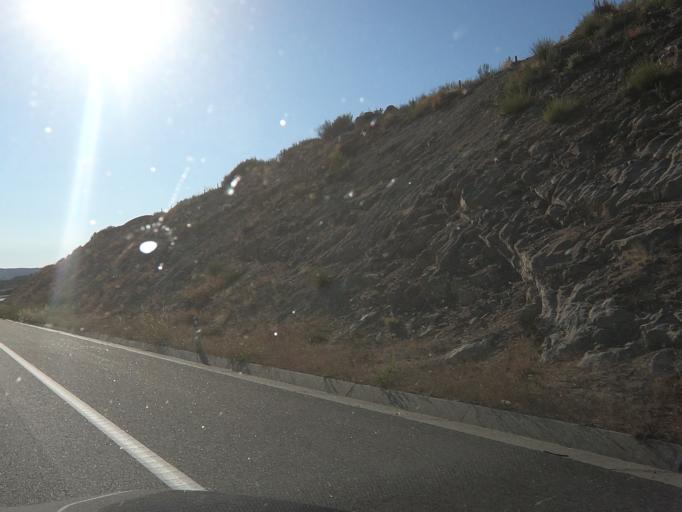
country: PT
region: Vila Real
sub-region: Murca
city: Murca
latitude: 41.3738
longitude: -7.5291
